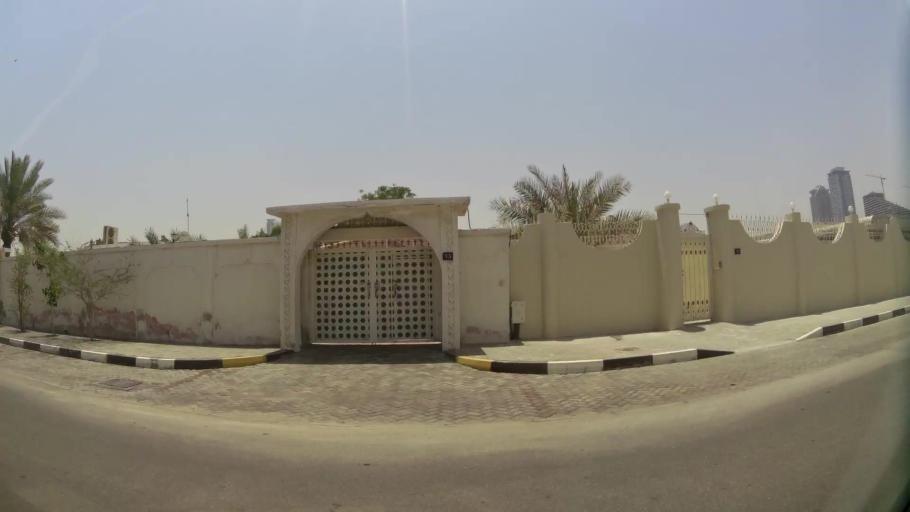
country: AE
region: Ash Shariqah
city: Sharjah
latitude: 25.3377
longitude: 55.3641
